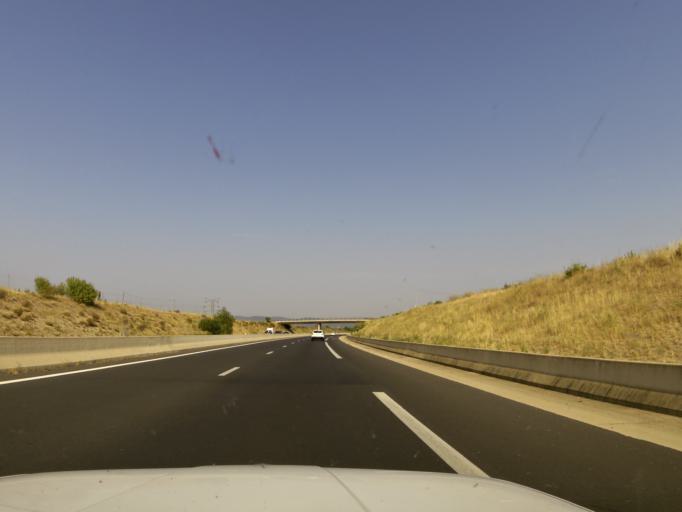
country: FR
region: Languedoc-Roussillon
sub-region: Departement de l'Herault
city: Saint-Andre-de-Sangonis
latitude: 43.6598
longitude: 3.5078
